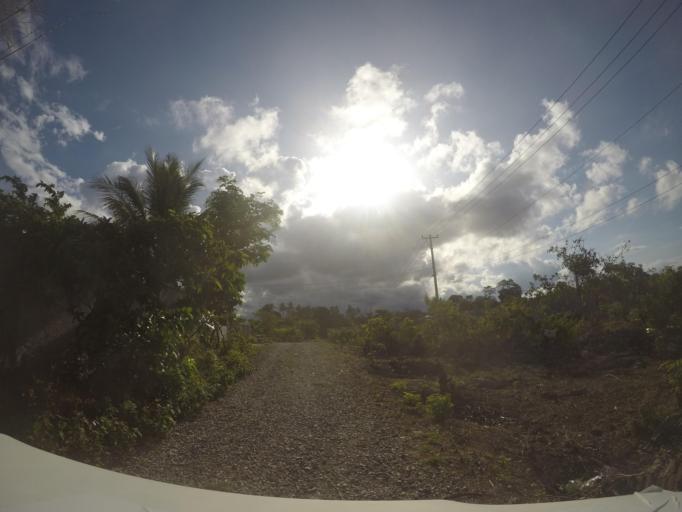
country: TL
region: Baucau
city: Baucau
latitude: -8.4745
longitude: 126.4633
